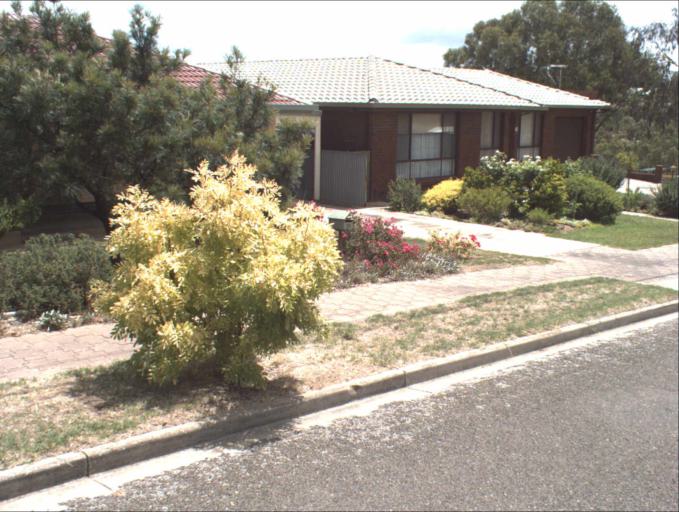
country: AU
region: South Australia
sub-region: Port Adelaide Enfield
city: Gilles Plains
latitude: -34.8419
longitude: 138.6523
